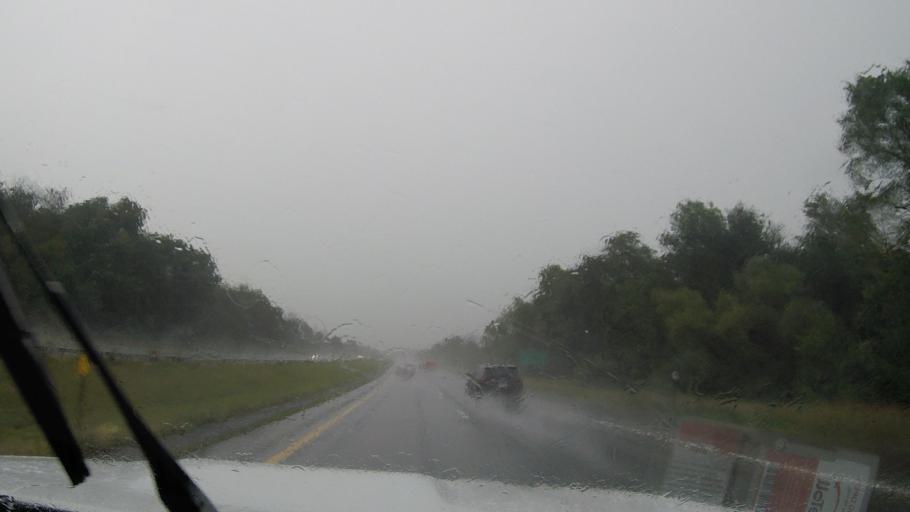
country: US
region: New York
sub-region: Seneca County
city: Waterloo
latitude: 42.9681
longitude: -76.8367
